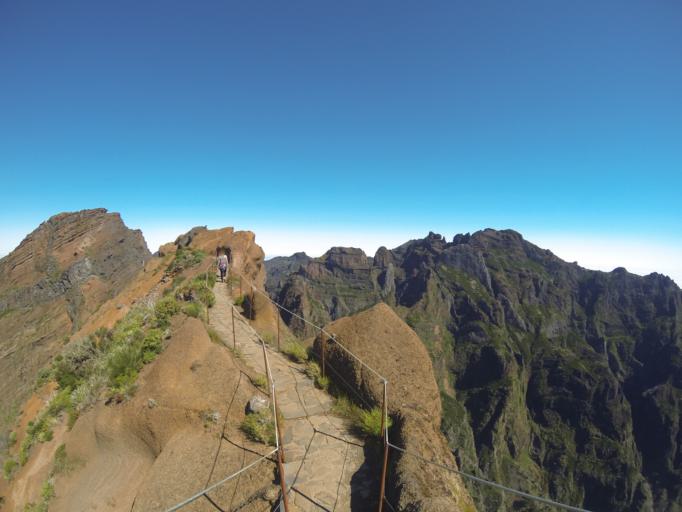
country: PT
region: Madeira
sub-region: Camara de Lobos
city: Curral das Freiras
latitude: 32.7387
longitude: -16.9352
